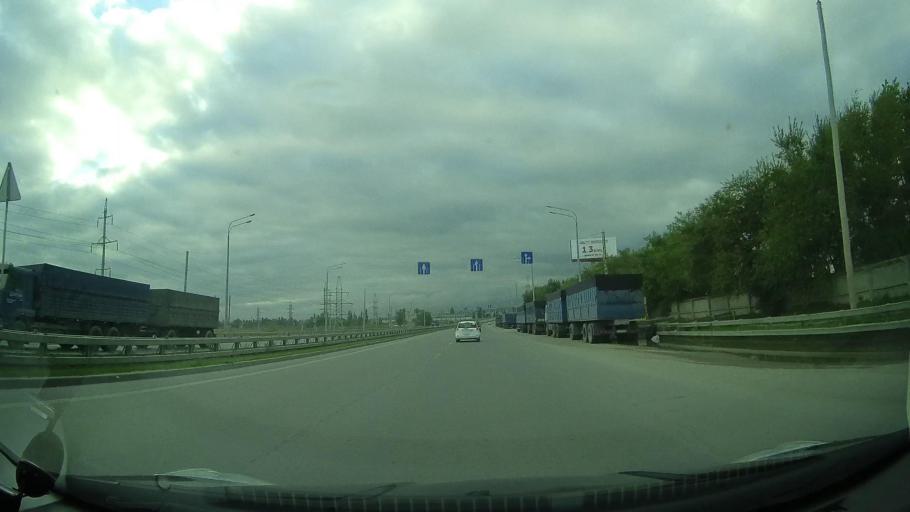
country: RU
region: Rostov
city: Rostov-na-Donu
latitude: 47.2024
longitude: 39.7186
